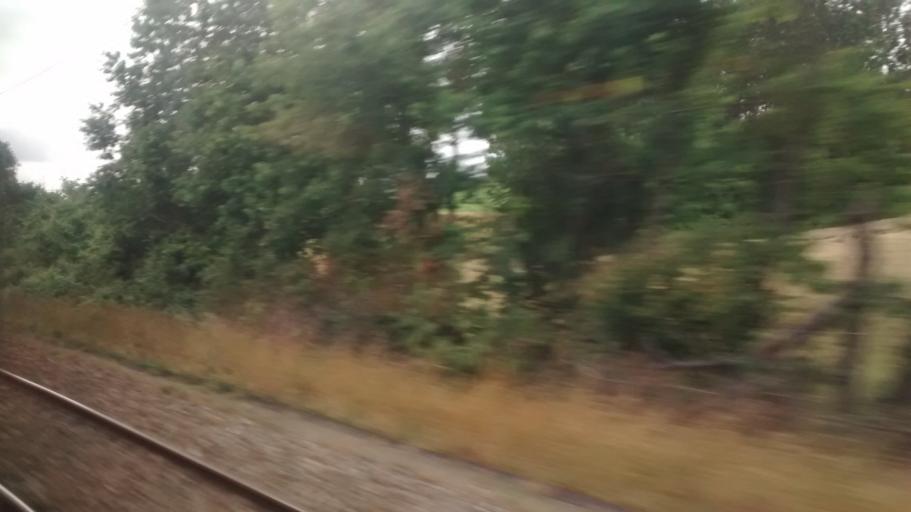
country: FR
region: Pays de la Loire
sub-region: Departement de la Mayenne
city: Argentre
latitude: 48.1294
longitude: -0.6158
